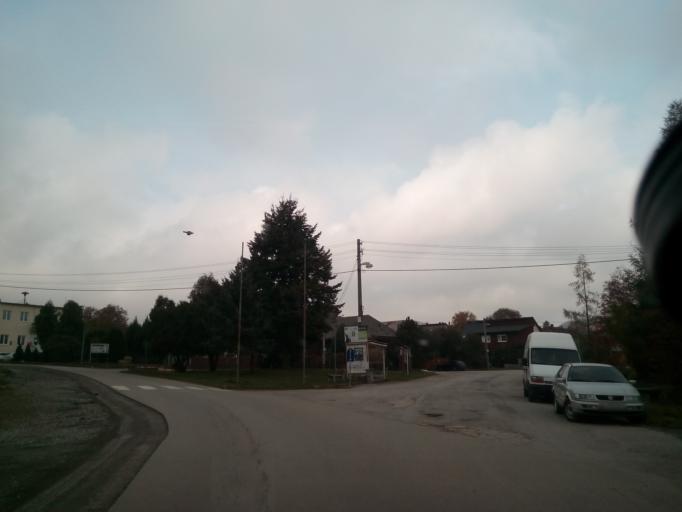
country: SK
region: Kosicky
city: Kosice
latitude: 48.7275
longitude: 21.1422
